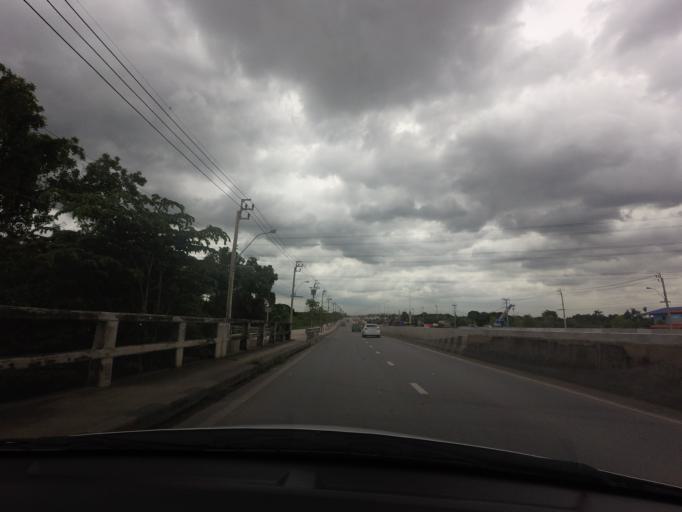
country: TH
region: Bangkok
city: Saphan Sung
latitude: 13.7537
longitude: 100.7048
